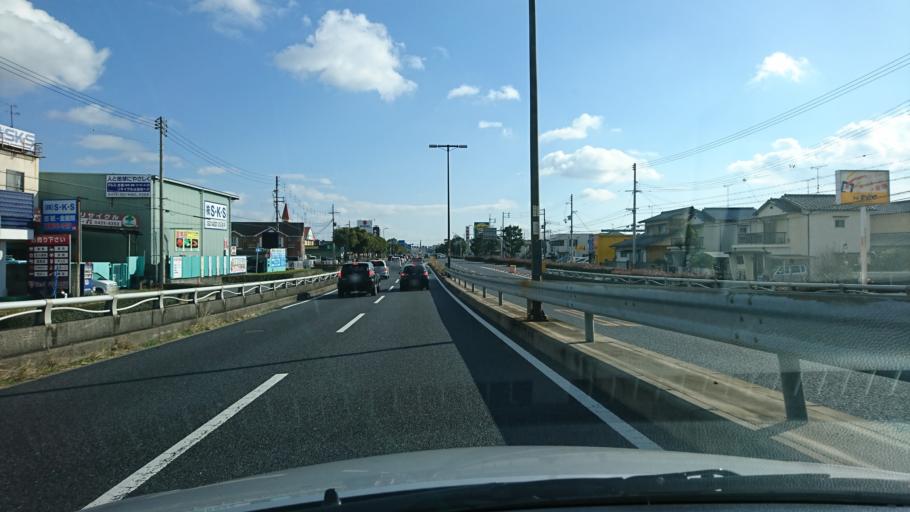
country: JP
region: Hyogo
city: Kakogawacho-honmachi
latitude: 34.7550
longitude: 134.8251
